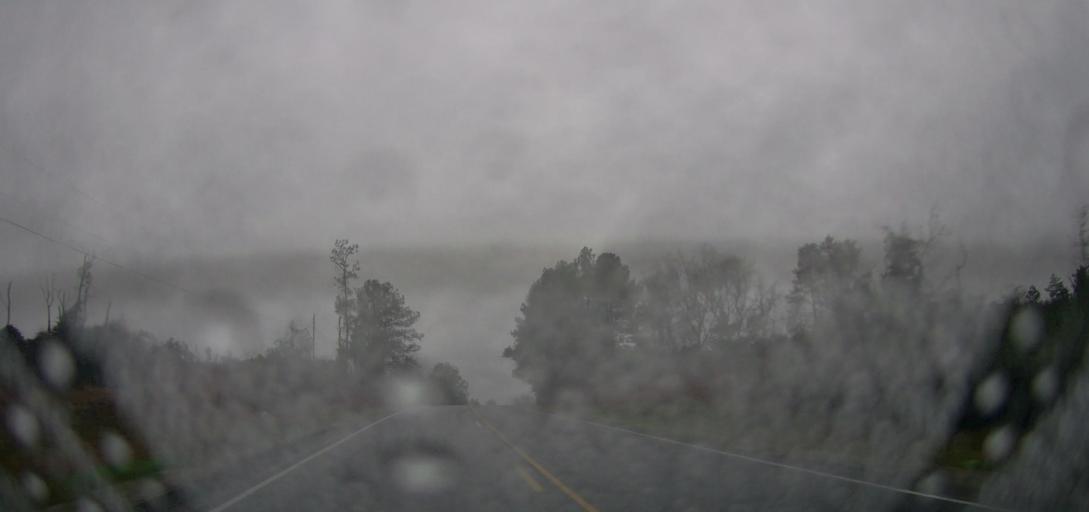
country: US
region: Alabama
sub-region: Chilton County
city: Clanton
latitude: 32.6413
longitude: -86.7544
